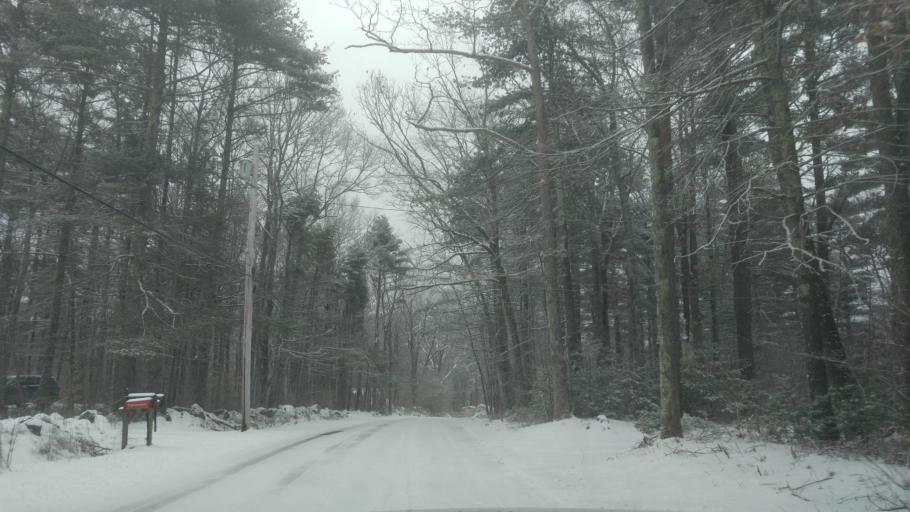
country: US
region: Rhode Island
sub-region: Providence County
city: Foster
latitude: 41.8239
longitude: -71.7236
